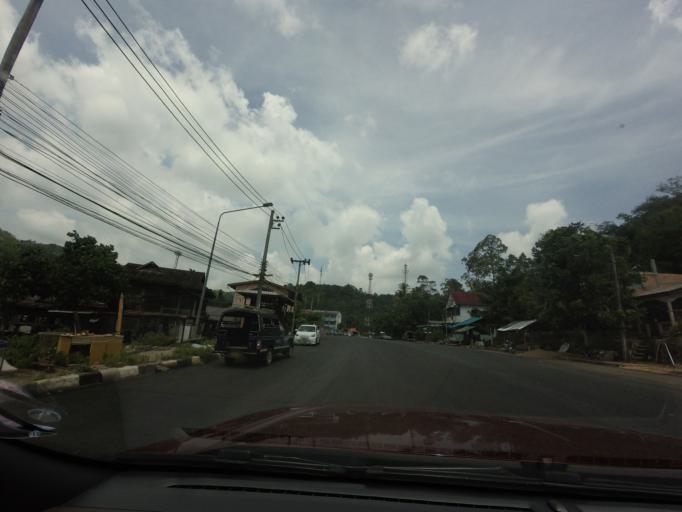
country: TH
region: Yala
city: Betong
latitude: 5.7495
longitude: 101.0372
